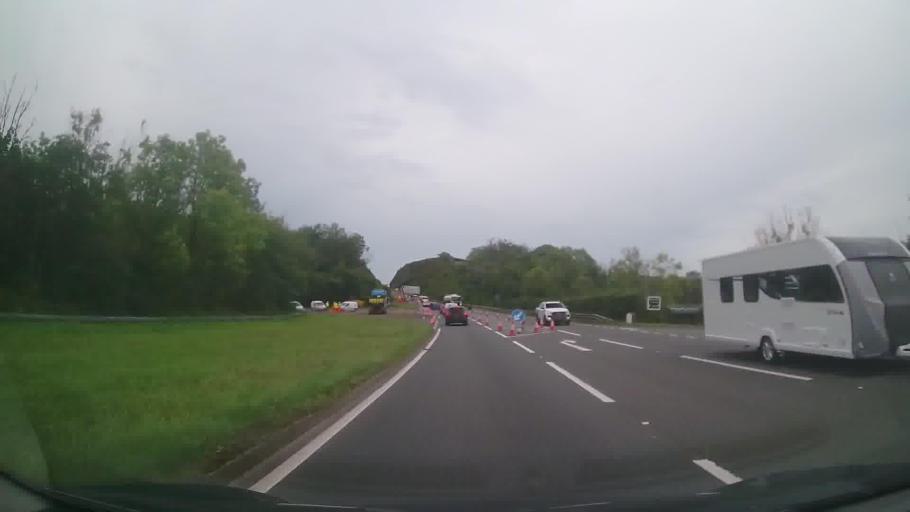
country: GB
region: Wales
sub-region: Pembrokeshire
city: Kilgetty
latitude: 51.7547
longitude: -4.6771
